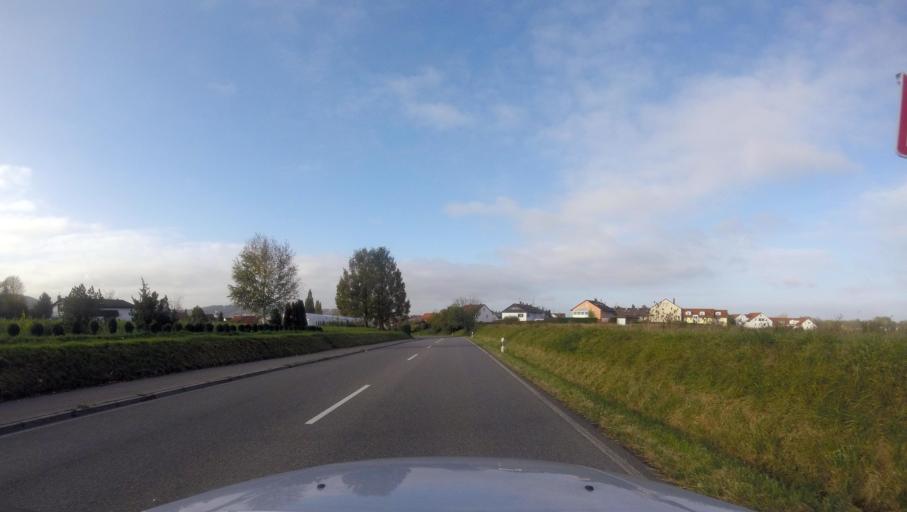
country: DE
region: Baden-Wuerttemberg
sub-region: Regierungsbezirk Stuttgart
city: Winnenden
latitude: 48.8815
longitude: 9.4073
